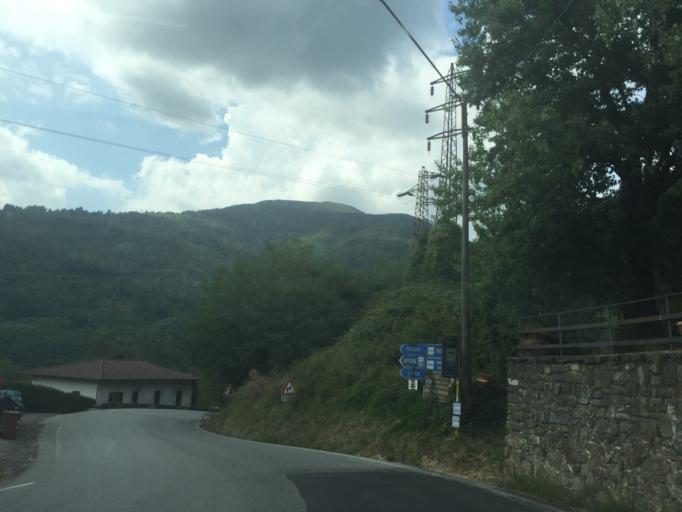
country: IT
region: Tuscany
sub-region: Provincia di Pistoia
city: San Marcello Pistoiese
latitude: 44.0576
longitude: 10.7715
